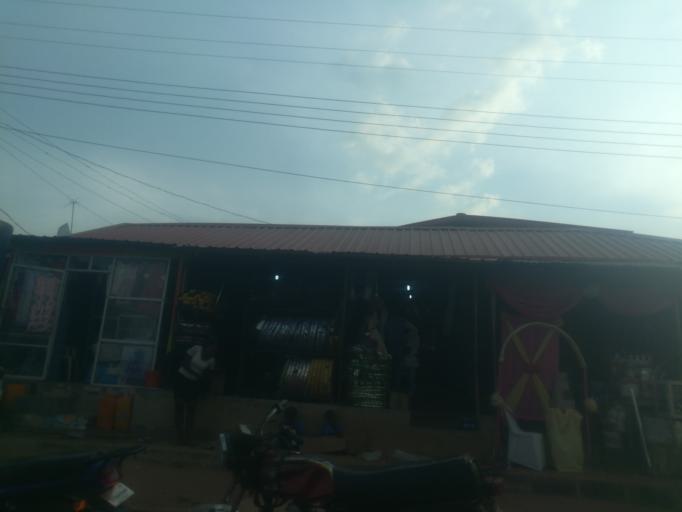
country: NG
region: Ogun
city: Abeokuta
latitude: 7.1634
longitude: 3.3135
